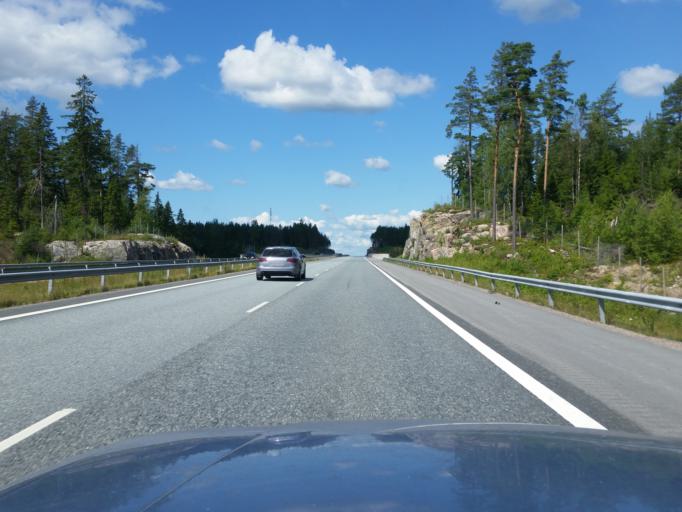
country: FI
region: Varsinais-Suomi
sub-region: Salo
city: Suomusjaervi
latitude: 60.3703
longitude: 23.6543
